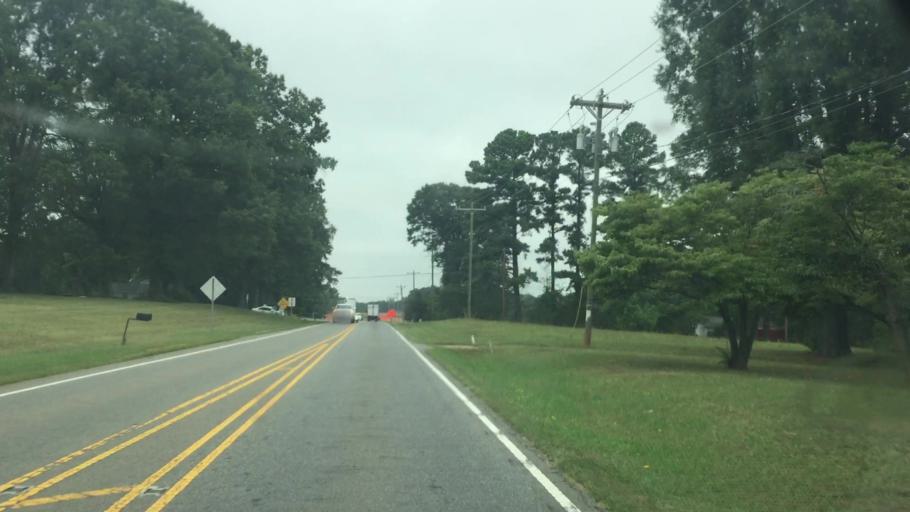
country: US
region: North Carolina
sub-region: Iredell County
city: Mooresville
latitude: 35.5464
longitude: -80.7713
